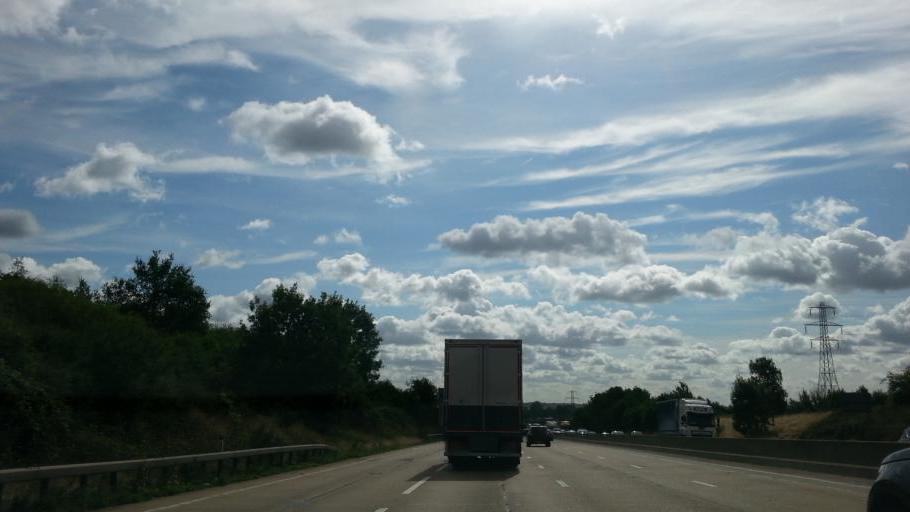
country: GB
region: England
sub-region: Greater London
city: Enfield
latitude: 51.6867
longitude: -0.0742
